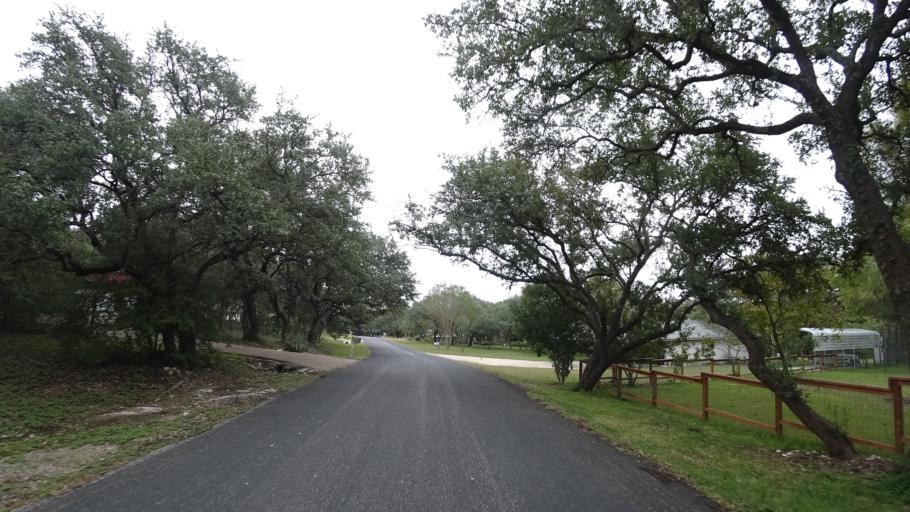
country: US
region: Texas
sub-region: Travis County
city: Barton Creek
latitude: 30.2359
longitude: -97.9021
